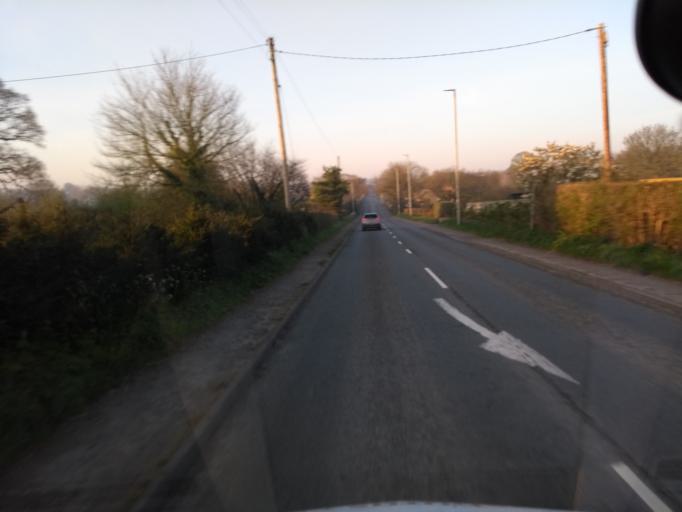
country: GB
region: England
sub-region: Somerset
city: Chard
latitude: 50.8870
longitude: -2.9505
